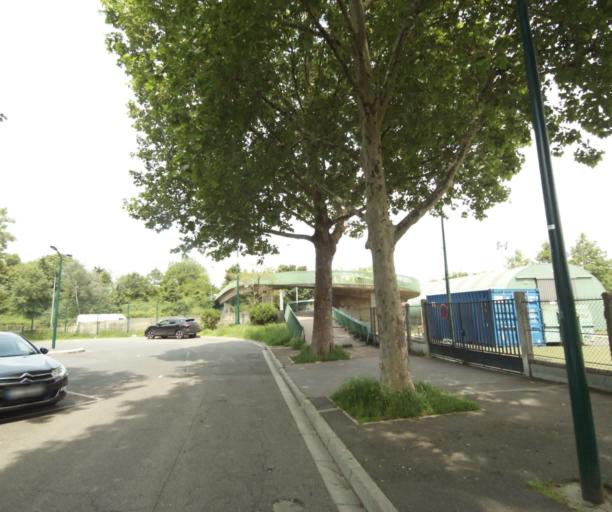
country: FR
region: Ile-de-France
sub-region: Departement du Val-d'Oise
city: Bezons
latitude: 48.9240
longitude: 2.2316
